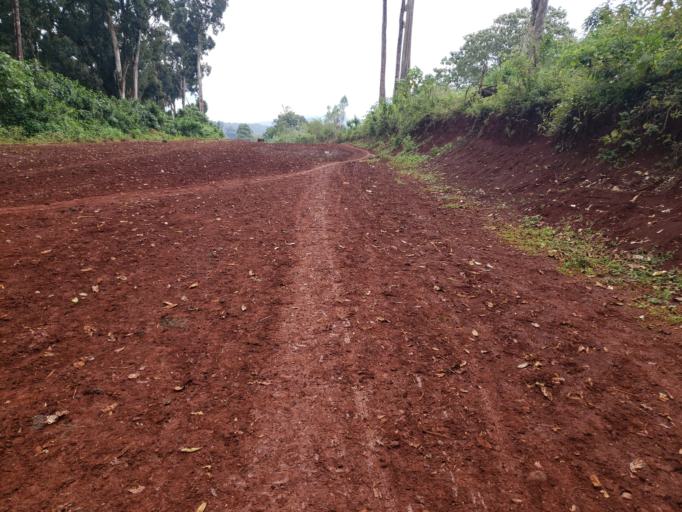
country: ET
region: Oromiya
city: Dodola
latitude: 6.5553
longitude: 39.4237
